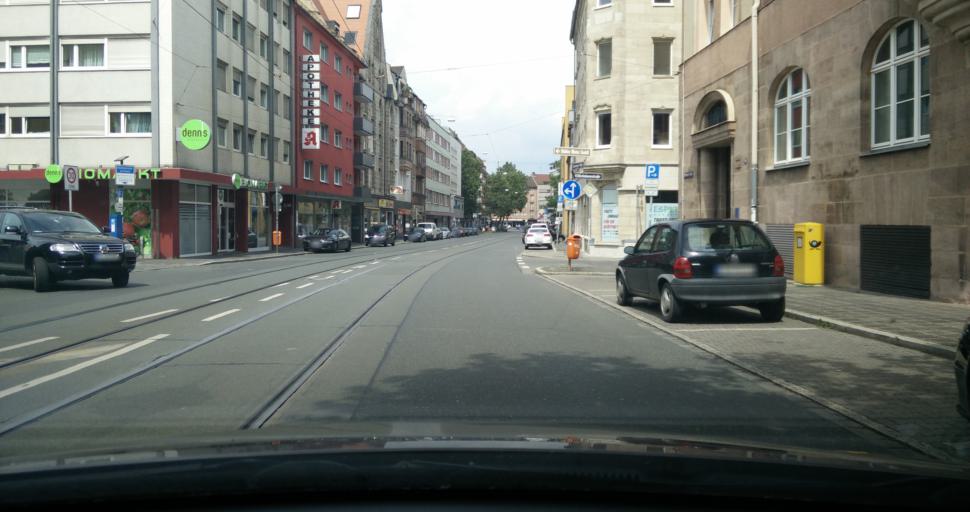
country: DE
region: Bavaria
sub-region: Regierungsbezirk Mittelfranken
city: Nuernberg
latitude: 49.4389
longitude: 11.0905
